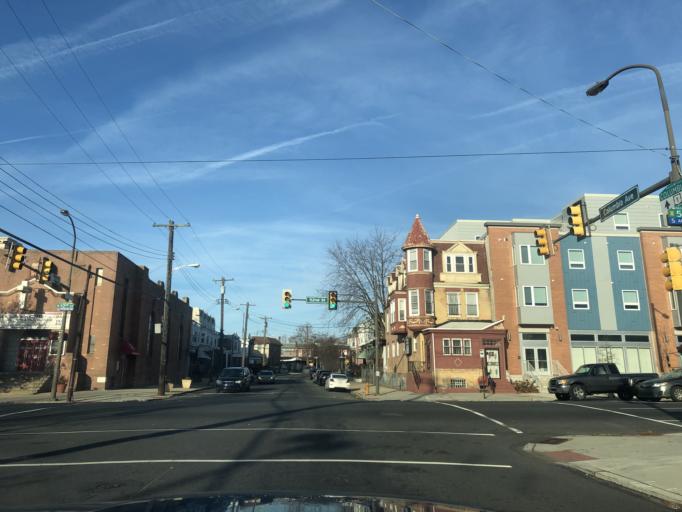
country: US
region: Pennsylvania
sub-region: Montgomery County
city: Bala-Cynwyd
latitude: 39.9803
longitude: -75.2245
